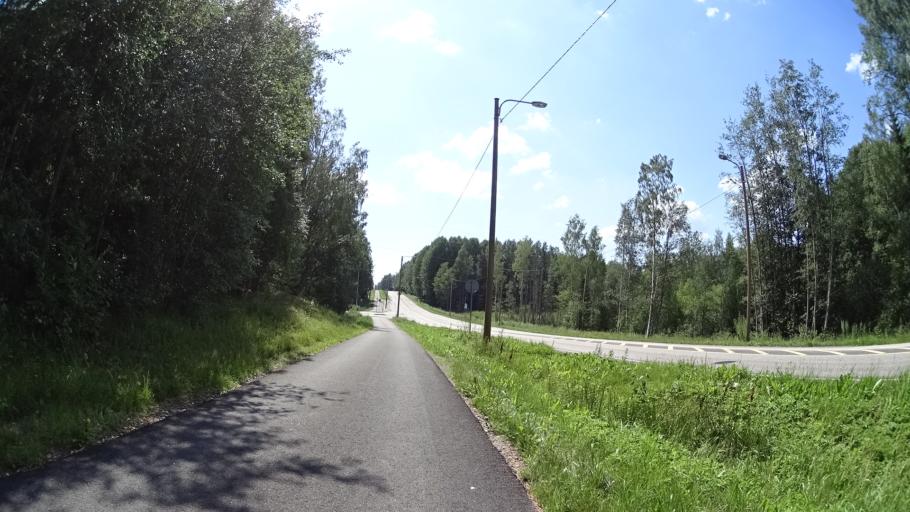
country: FI
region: Uusimaa
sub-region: Helsinki
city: Vantaa
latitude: 60.3301
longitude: 25.0031
